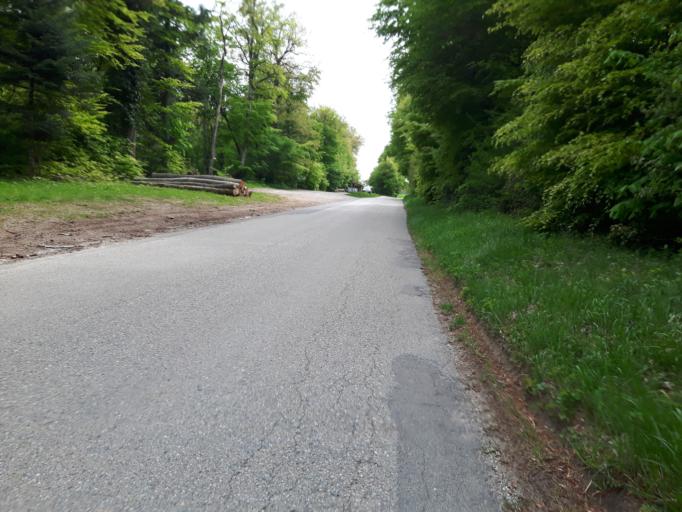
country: CH
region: Neuchatel
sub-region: Boudry District
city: Bevaix
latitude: 46.9218
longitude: 6.8021
